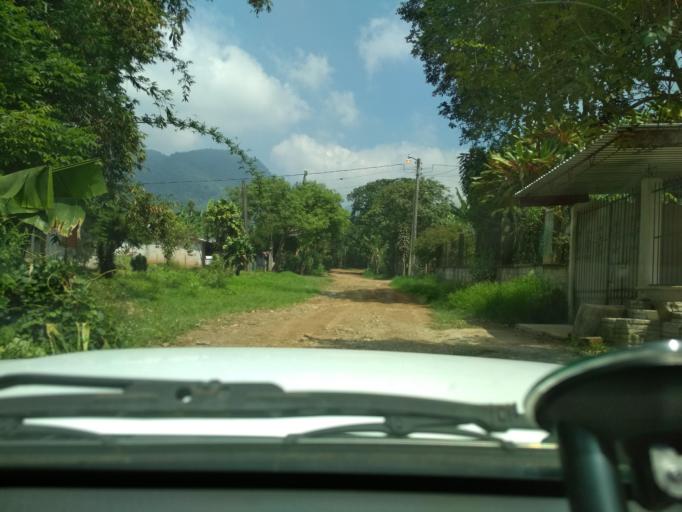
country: MX
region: Veracruz
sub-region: Fortin
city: Santa Lucia Potrerillo
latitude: 18.9674
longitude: -97.0255
